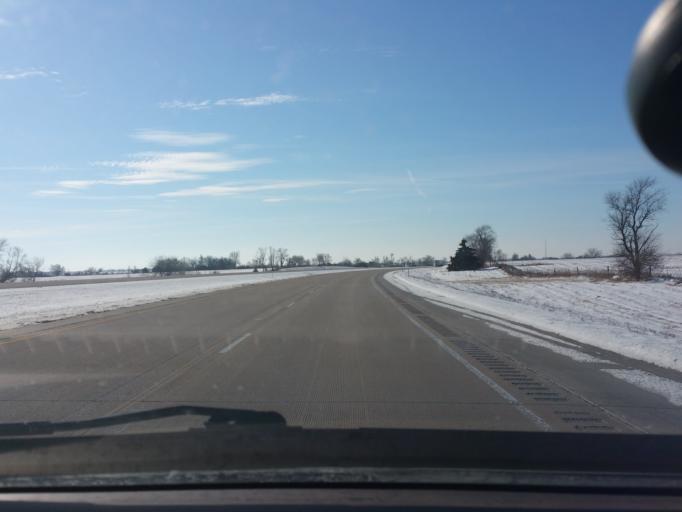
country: US
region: Iowa
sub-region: Decatur County
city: Leon
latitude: 40.8427
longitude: -93.8053
